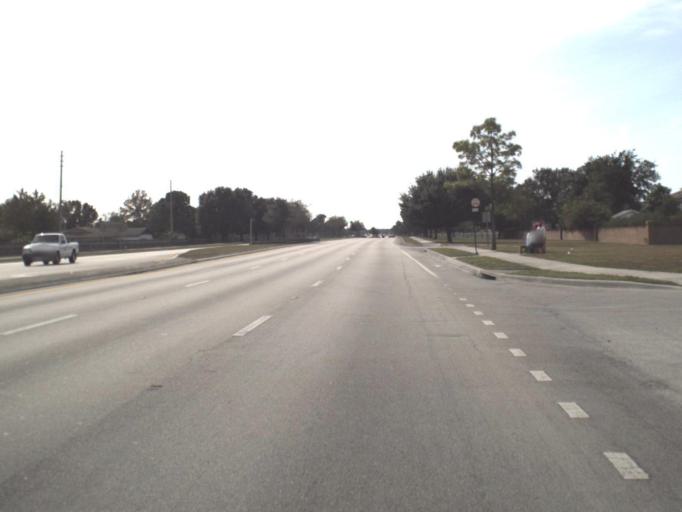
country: US
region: Florida
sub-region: Orange County
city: Oak Ridge
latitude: 28.4857
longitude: -81.4176
